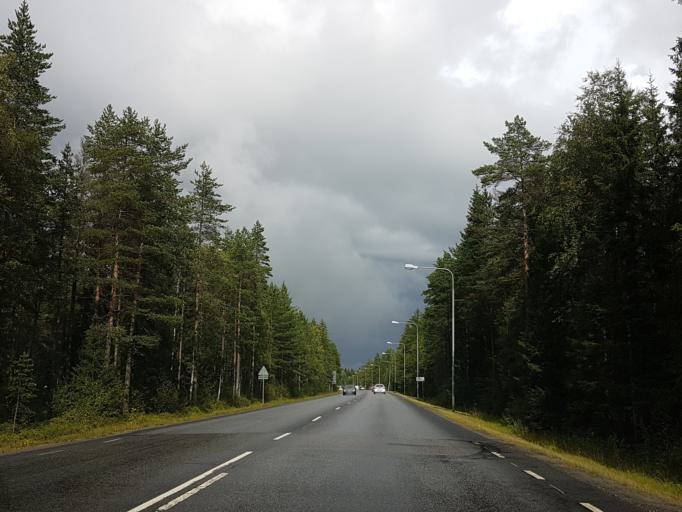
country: SE
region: Vaesterbotten
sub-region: Umea Kommun
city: Ersmark
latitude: 63.8484
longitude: 20.3423
